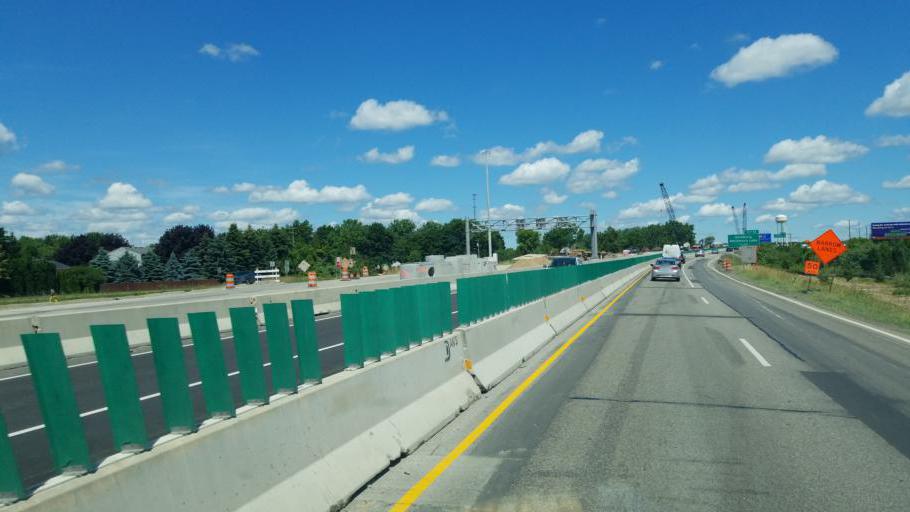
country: US
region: Michigan
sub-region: Livingston County
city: Whitmore Lake
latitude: 42.4208
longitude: -83.7676
